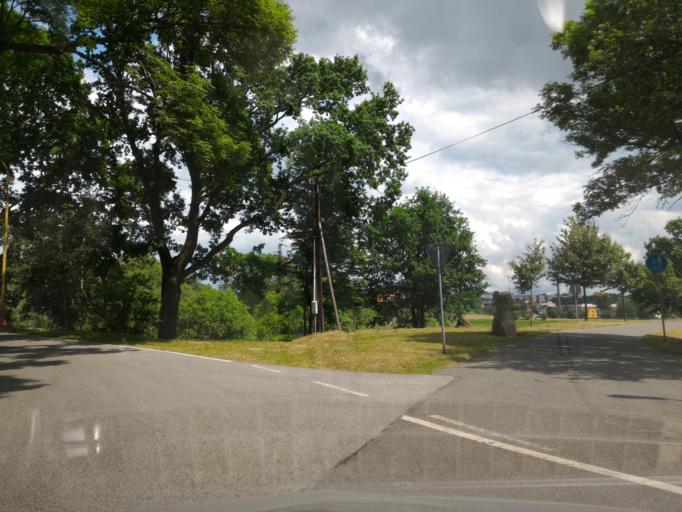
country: CZ
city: Hradek nad Nisou
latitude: 50.8538
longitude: 14.8320
